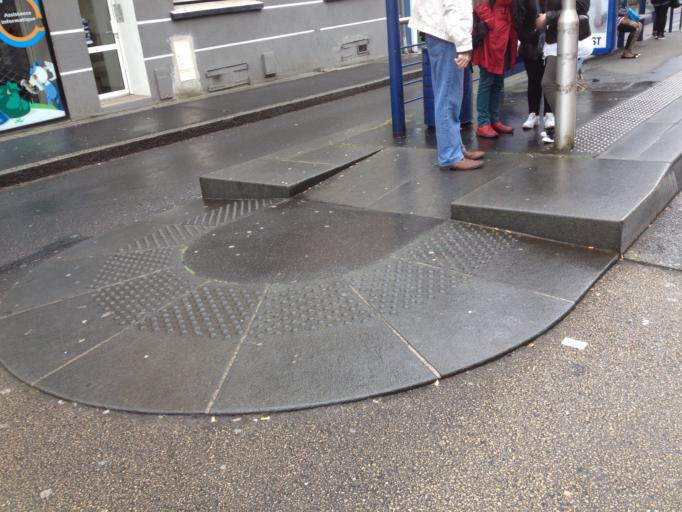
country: FR
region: Brittany
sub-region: Departement du Finistere
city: Brest
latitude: 48.3960
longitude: -4.4839
